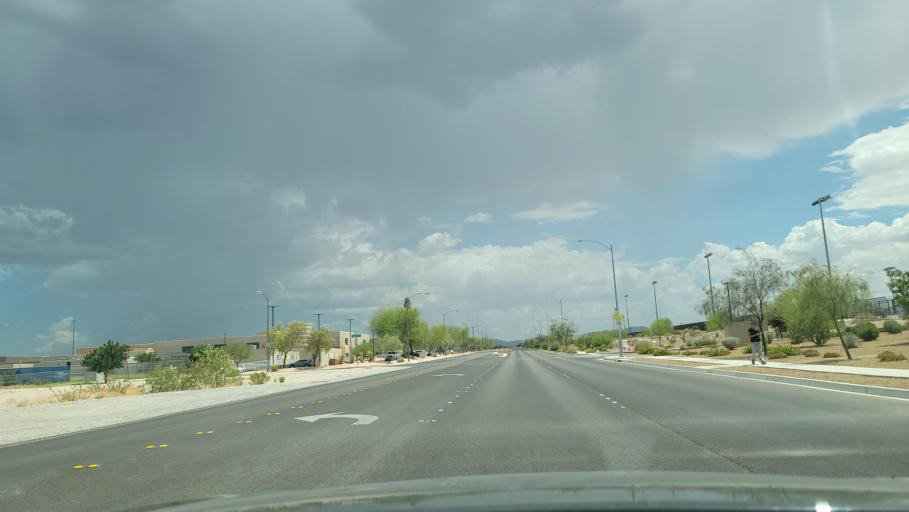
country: US
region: Nevada
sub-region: Clark County
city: Enterprise
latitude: 36.0527
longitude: -115.2702
